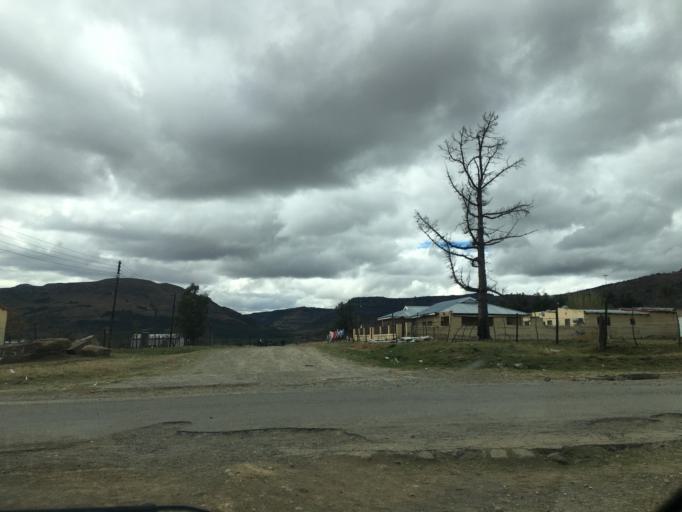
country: ZA
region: Eastern Cape
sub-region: Chris Hani District Municipality
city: Cala
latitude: -31.5237
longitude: 27.6906
